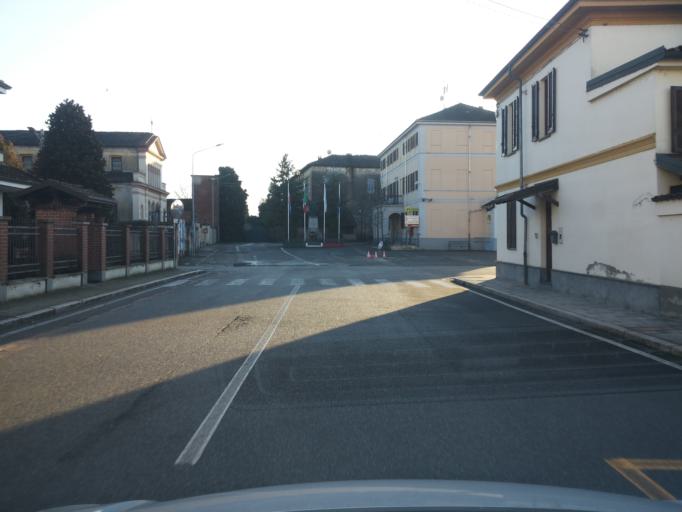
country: IT
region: Piedmont
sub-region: Provincia di Vercelli
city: Lignana
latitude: 45.2857
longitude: 8.3464
